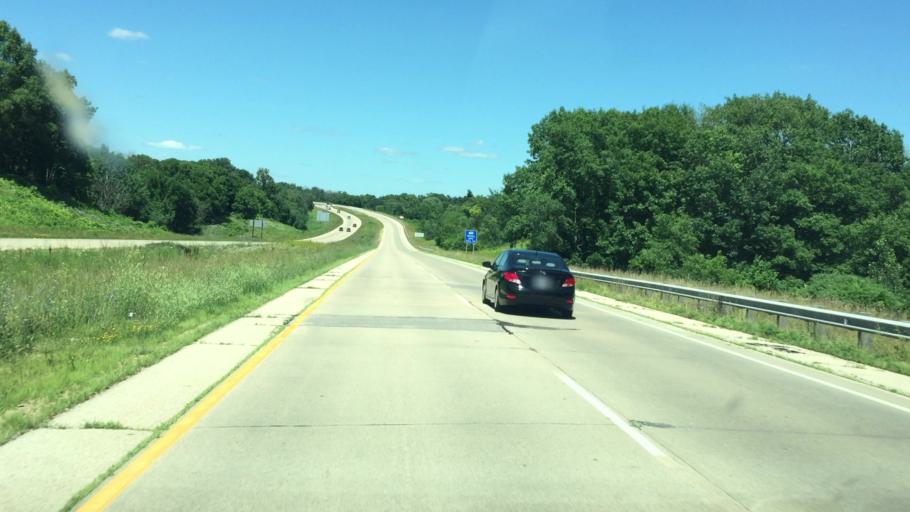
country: US
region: Illinois
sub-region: Jo Daviess County
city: East Dubuque
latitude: 42.5359
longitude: -90.6108
